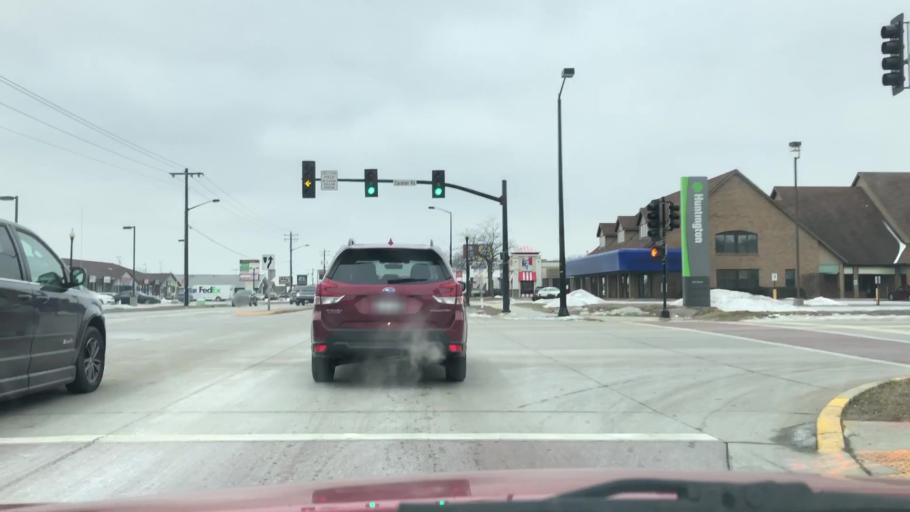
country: US
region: Wisconsin
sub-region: Brown County
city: Ashwaubenon
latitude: 44.4897
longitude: -88.0651
